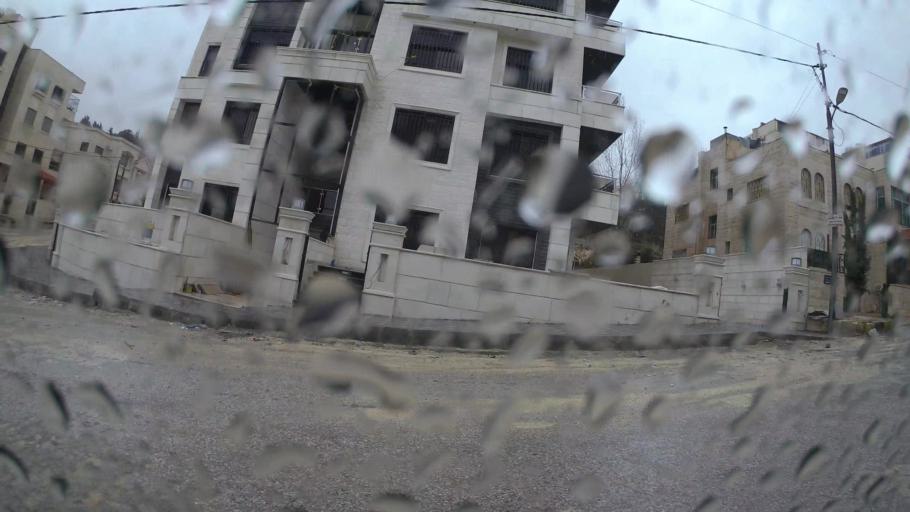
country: JO
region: Amman
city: Al Jubayhah
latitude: 32.0173
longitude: 35.8944
